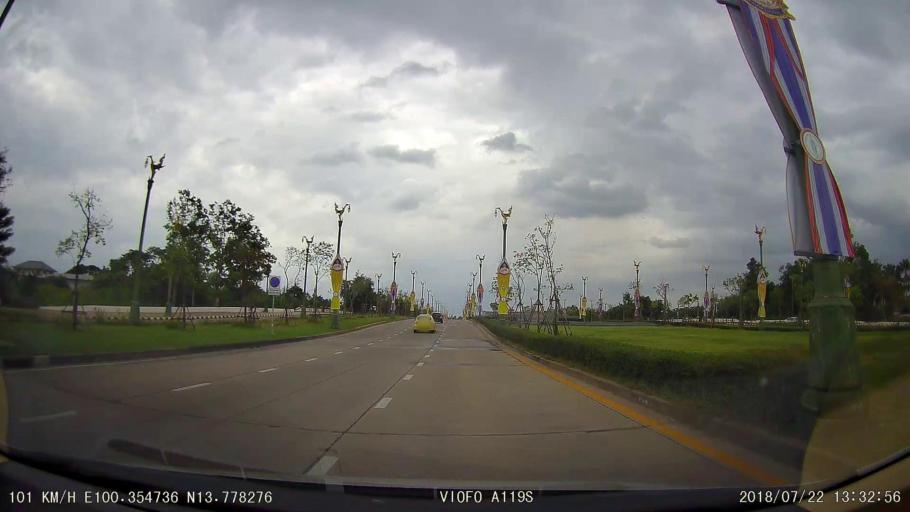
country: TH
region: Bangkok
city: Thawi Watthana
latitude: 13.7783
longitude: 100.3549
